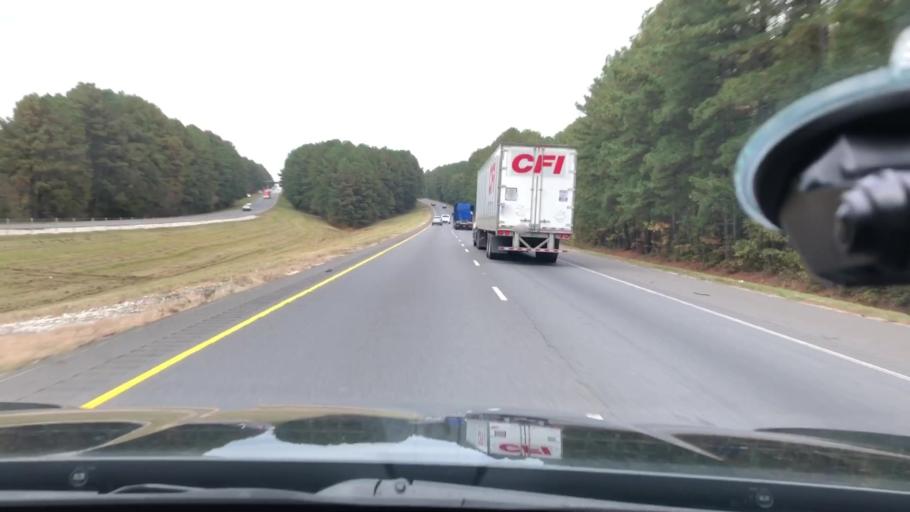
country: US
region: Arkansas
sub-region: Hot Spring County
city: Malvern
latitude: 34.2819
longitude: -92.9595
